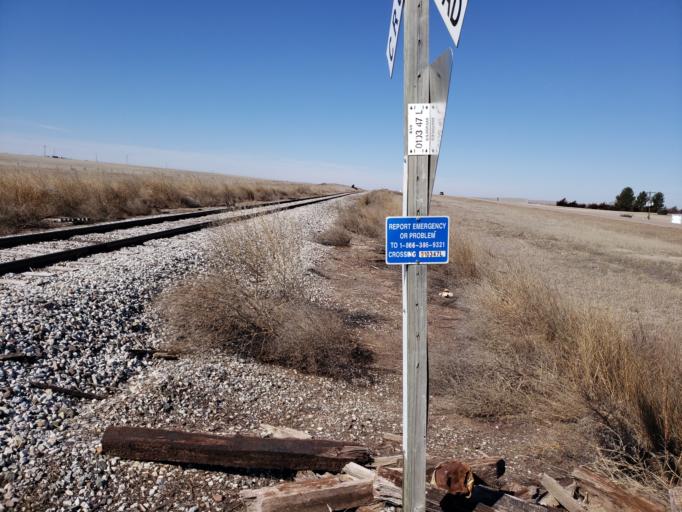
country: US
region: Kansas
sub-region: Ness County
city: Ness City
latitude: 38.4507
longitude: -99.9723
